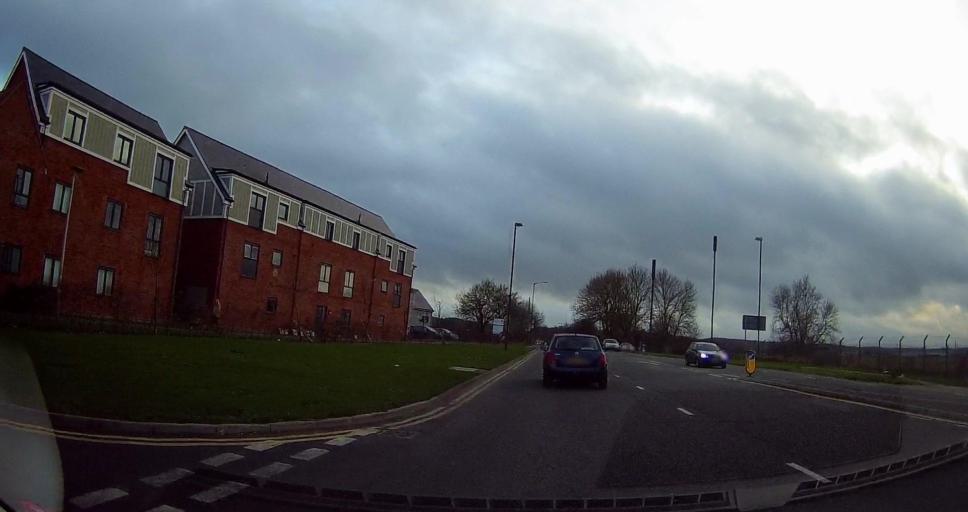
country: GB
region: England
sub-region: Kent
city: Chatham
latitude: 51.3565
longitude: 0.5091
